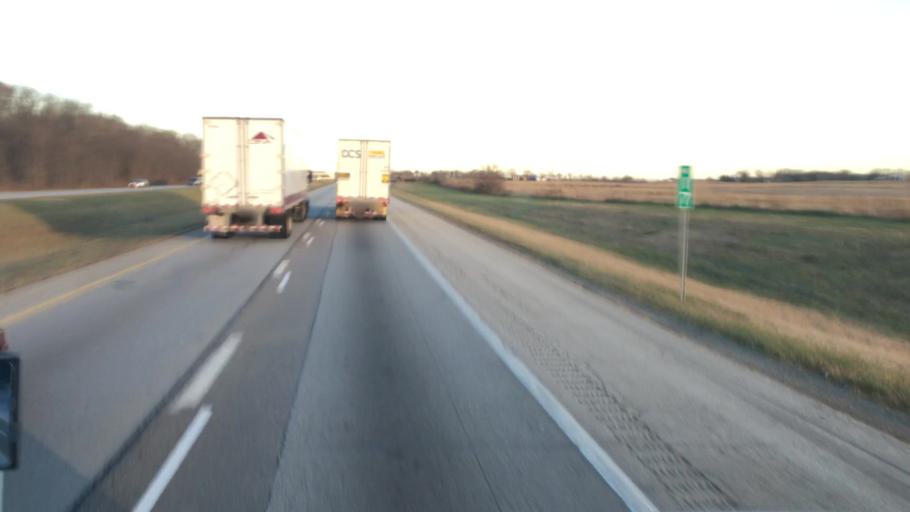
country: US
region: Ohio
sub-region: Preble County
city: Lewisburg
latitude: 39.8376
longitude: -84.4965
